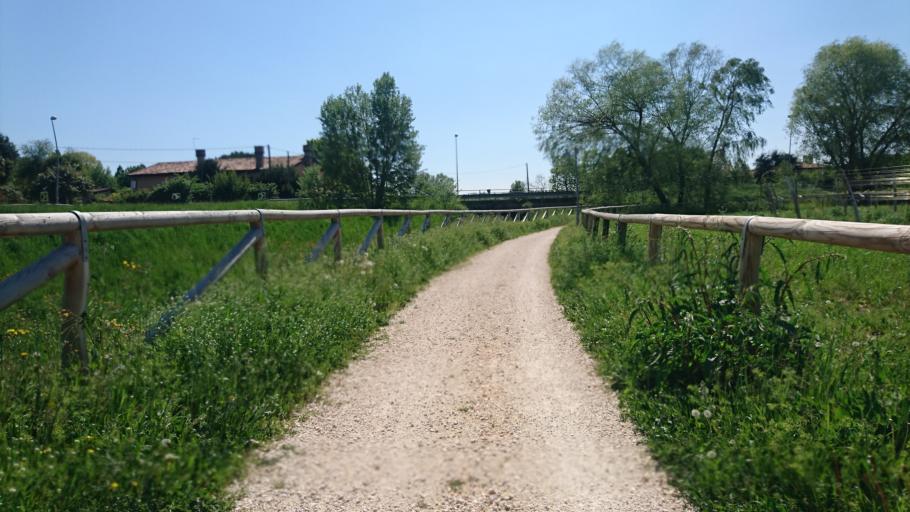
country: IT
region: Veneto
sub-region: Provincia di Treviso
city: Dosson
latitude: 45.6298
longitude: 12.2698
